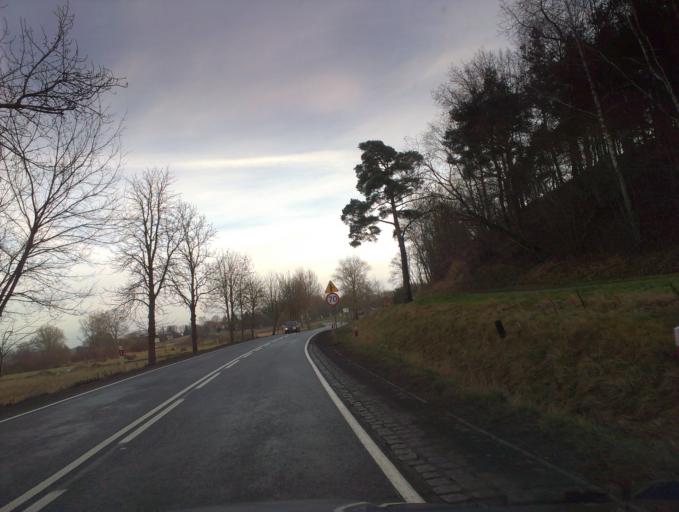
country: PL
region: West Pomeranian Voivodeship
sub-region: Powiat szczecinecki
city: Szczecinek
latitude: 53.7155
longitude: 16.7272
